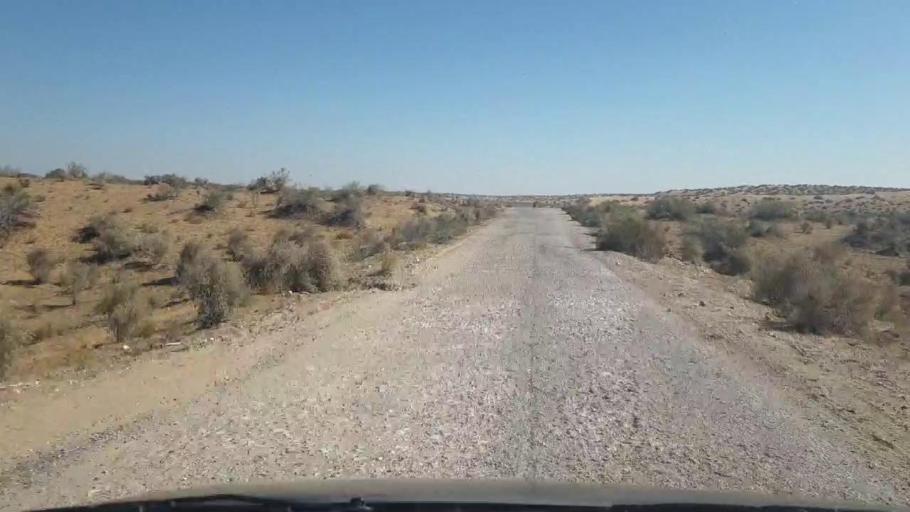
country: PK
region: Sindh
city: Bozdar
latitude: 27.0027
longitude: 68.8426
